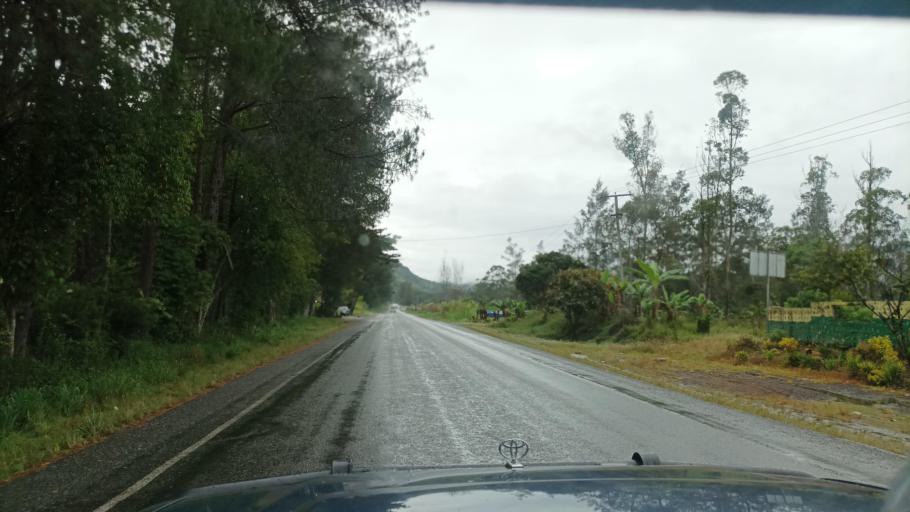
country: PG
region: Western Highlands
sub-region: Hagen
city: Mount Hagen
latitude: -5.8359
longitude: 144.3358
